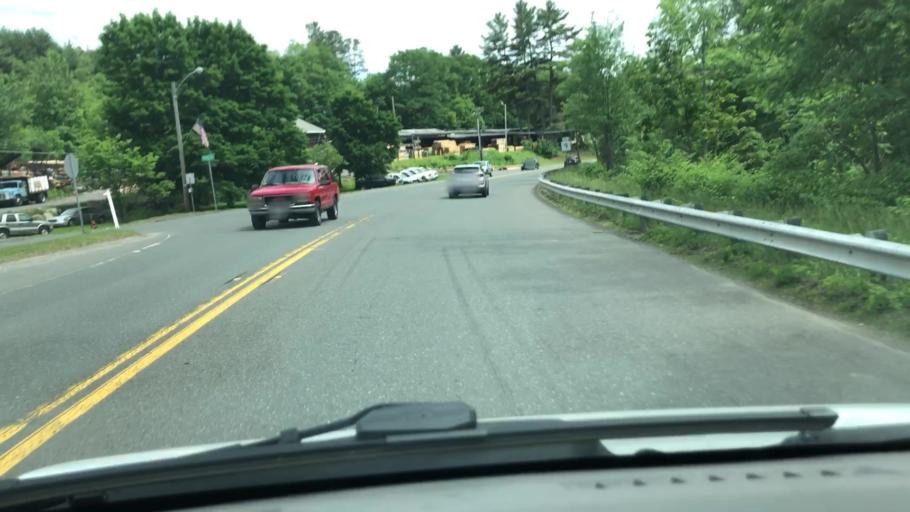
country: US
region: Massachusetts
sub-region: Hampshire County
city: Williamsburg
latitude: 42.3878
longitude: -72.7180
